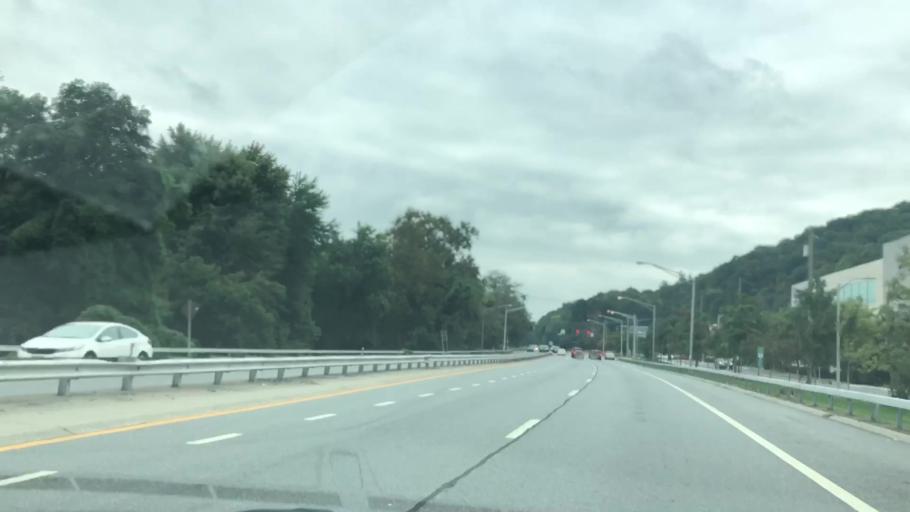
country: US
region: New York
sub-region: Westchester County
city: Ardsley
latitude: 41.0042
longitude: -73.8556
